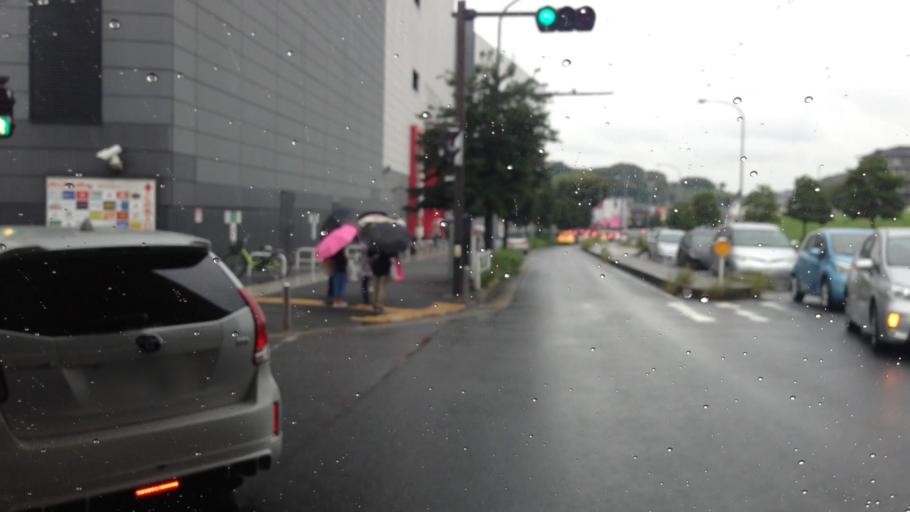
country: JP
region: Tokyo
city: Chofugaoka
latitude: 35.5504
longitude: 139.5769
